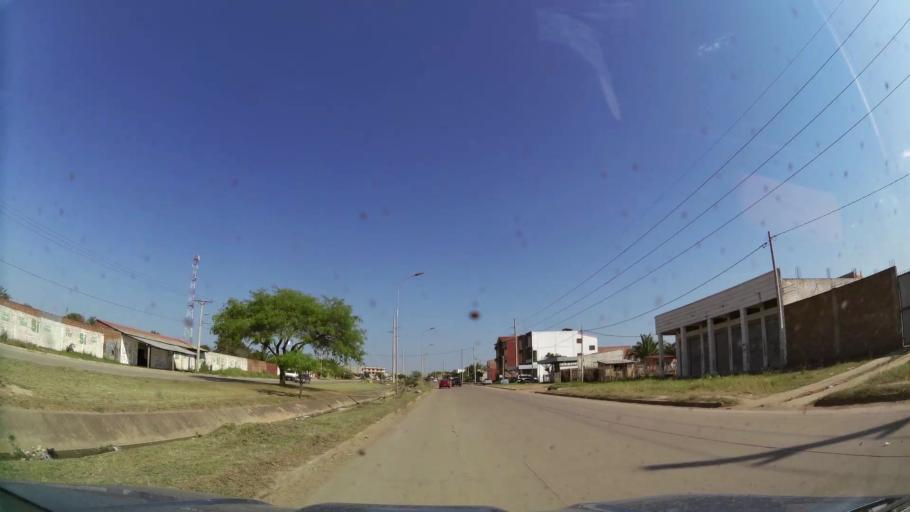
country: BO
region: Santa Cruz
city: Cotoca
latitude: -17.7794
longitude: -63.1079
